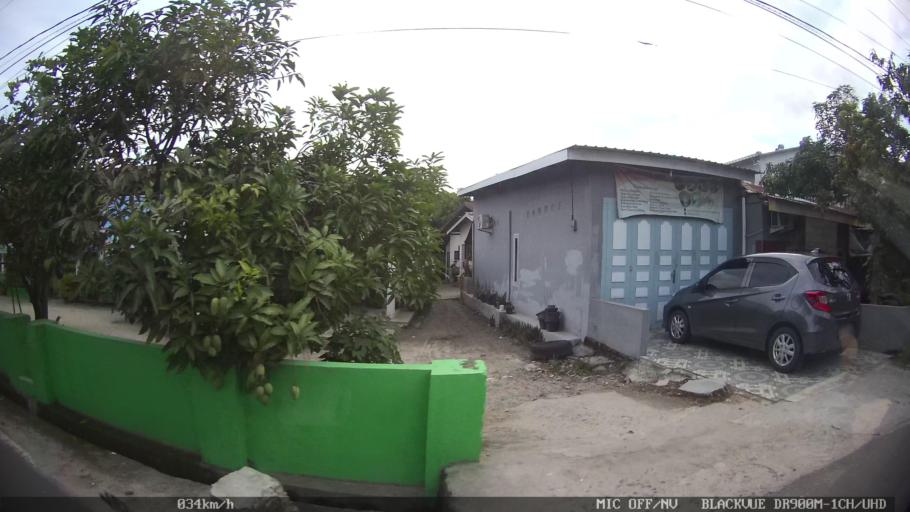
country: ID
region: North Sumatra
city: Percut
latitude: 3.6069
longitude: 98.8537
